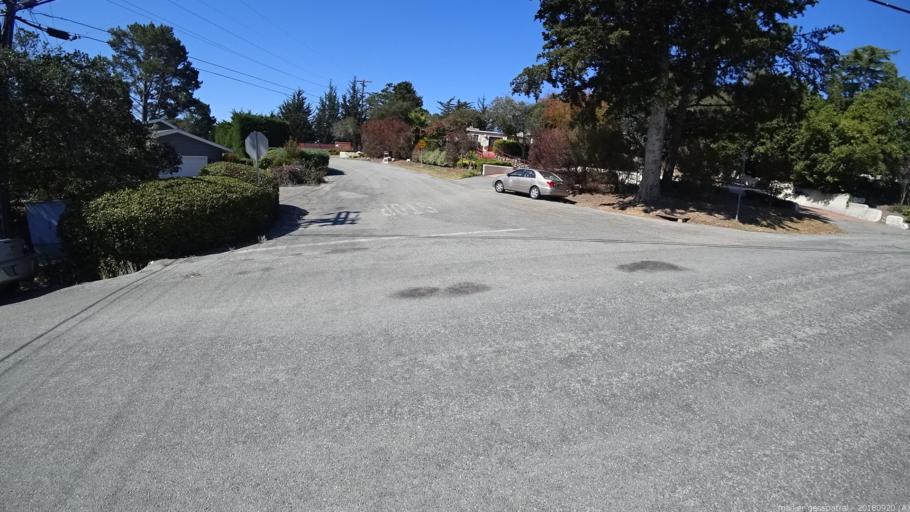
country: US
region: California
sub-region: Monterey County
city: Carmel-by-the-Sea
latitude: 36.5505
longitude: -121.9094
